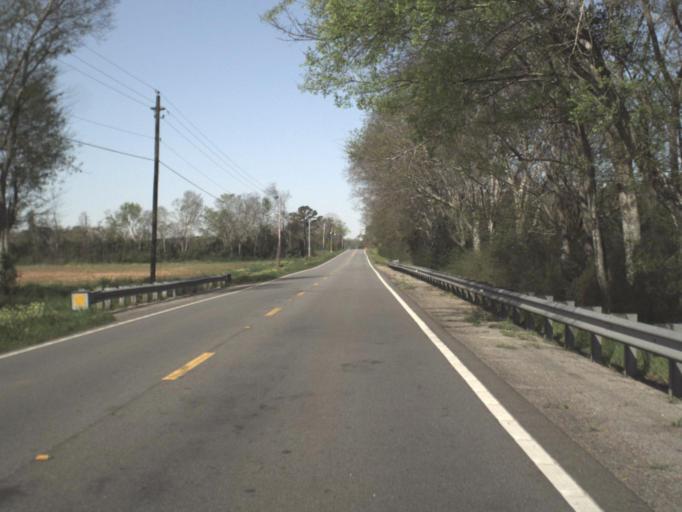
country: US
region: Florida
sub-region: Jackson County
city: Graceville
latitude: 30.9531
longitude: -85.4395
